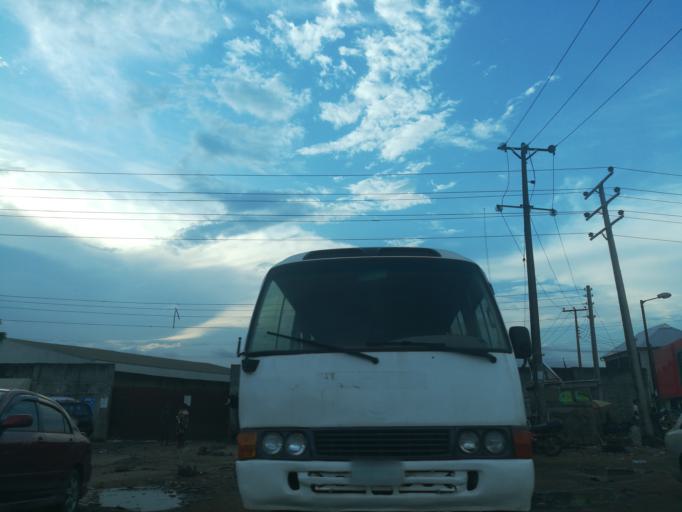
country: NG
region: Lagos
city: Ebute Ikorodu
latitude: 6.6231
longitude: 3.4823
